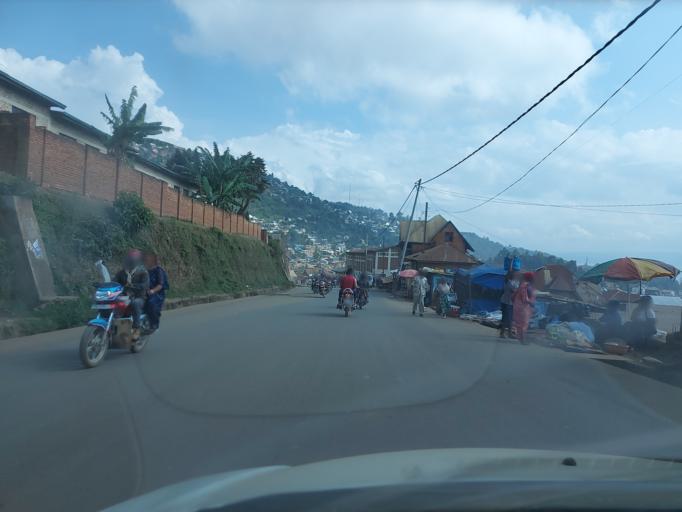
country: CD
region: South Kivu
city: Bukavu
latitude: -2.5165
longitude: 28.8504
